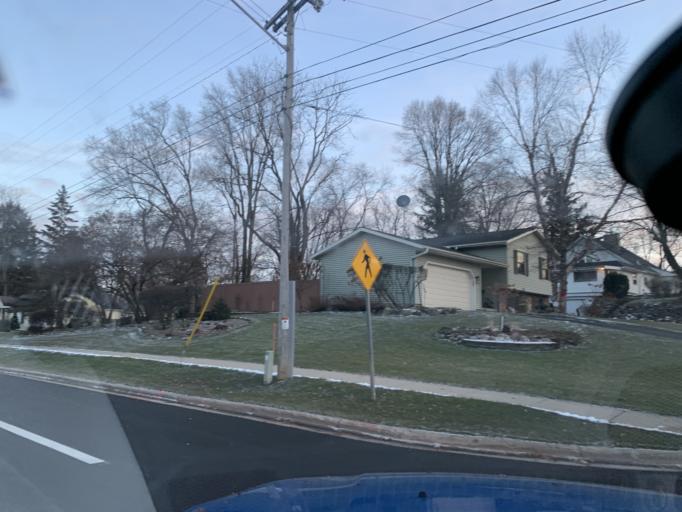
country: US
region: Wisconsin
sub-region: Dane County
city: Shorewood Hills
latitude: 43.0318
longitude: -89.4637
